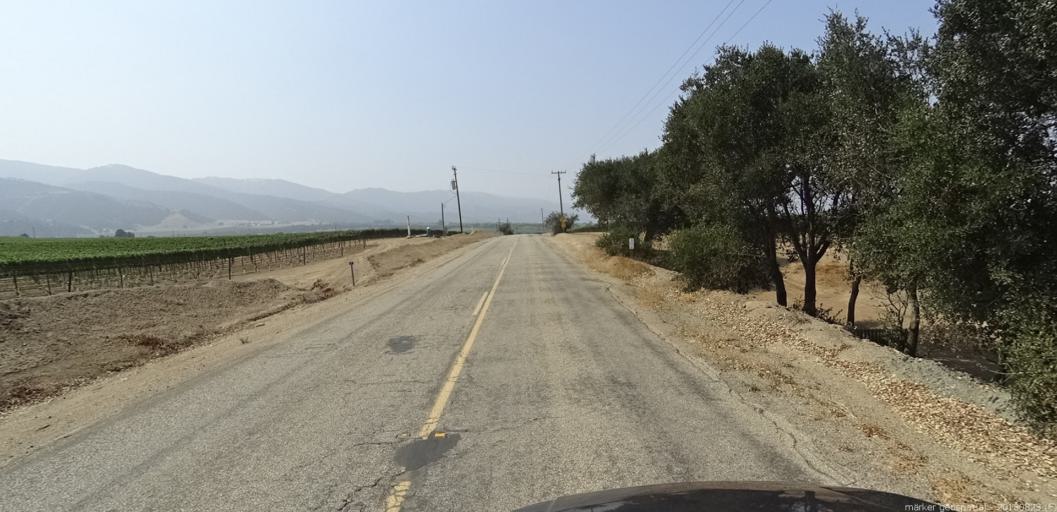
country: US
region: California
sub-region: Monterey County
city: Gonzales
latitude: 36.4373
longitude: -121.4282
